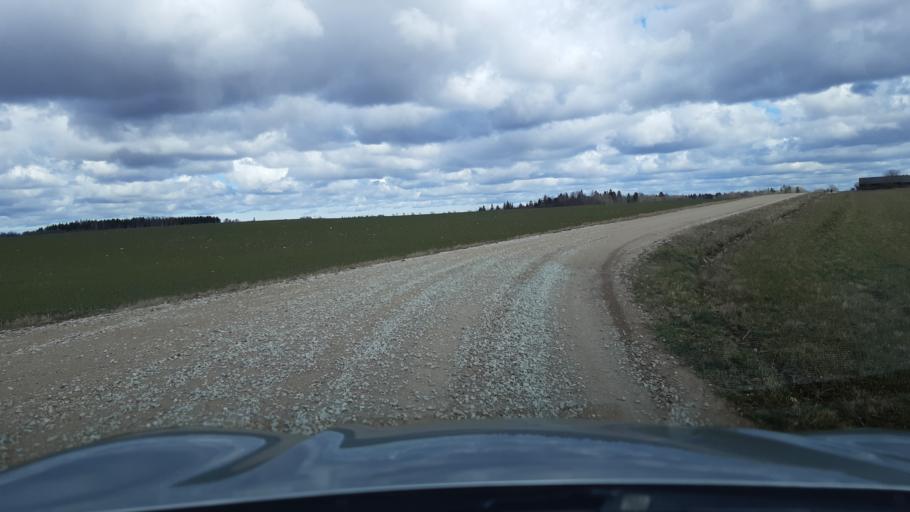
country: EE
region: Harju
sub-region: Rae vald
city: Vaida
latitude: 59.0715
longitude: 25.0943
